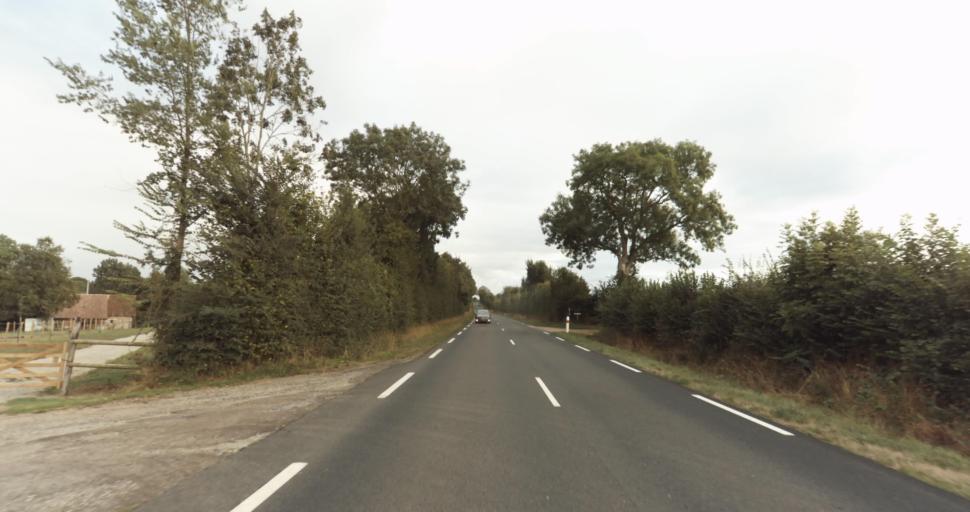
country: FR
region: Lower Normandy
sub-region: Departement de l'Orne
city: Vimoutiers
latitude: 48.8973
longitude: 0.2548
